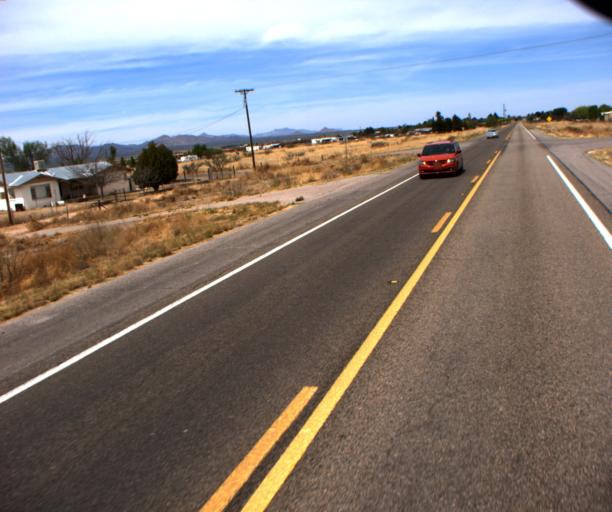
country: US
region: Arizona
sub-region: Cochise County
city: Bisbee
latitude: 31.6703
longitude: -109.6824
